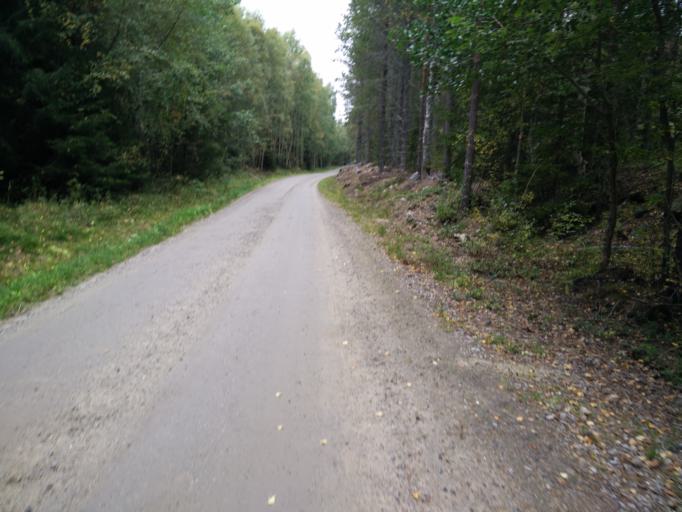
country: SE
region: Gaevleborg
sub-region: Hudiksvalls Kommun
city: Hudiksvall
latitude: 61.8332
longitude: 17.3325
